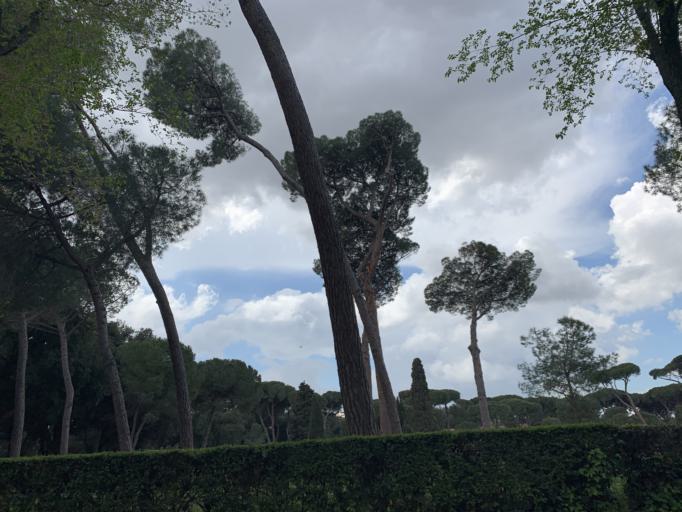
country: IT
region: Latium
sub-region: Citta metropolitana di Roma Capitale
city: Rome
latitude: 41.9137
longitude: 12.4888
